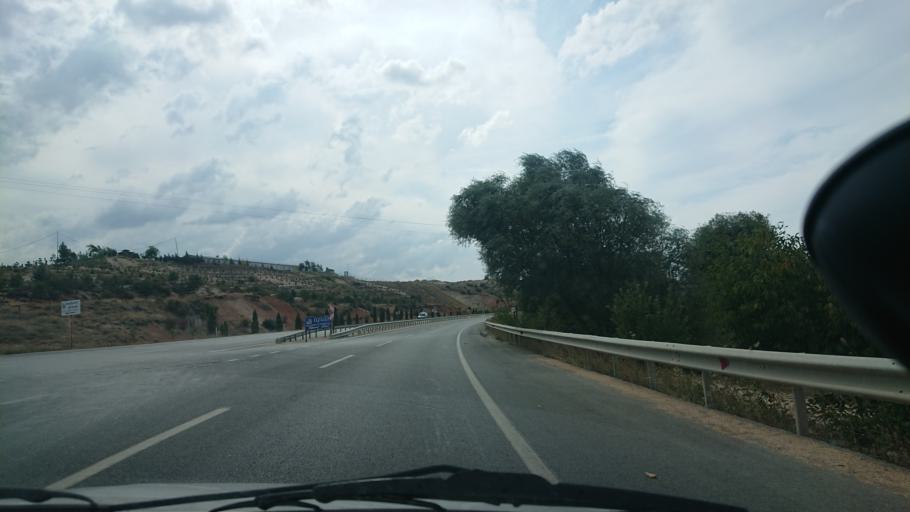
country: TR
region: Eskisehir
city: Eskisehir
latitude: 39.7275
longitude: 30.3744
